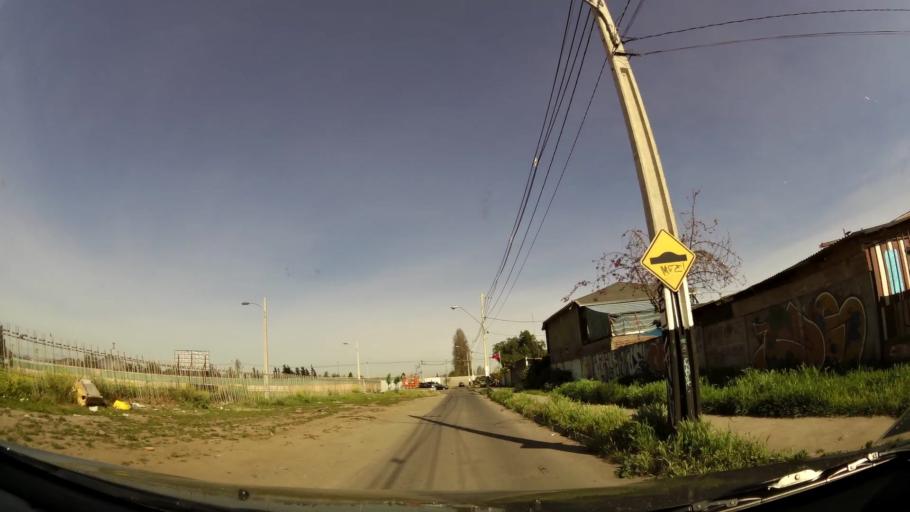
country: CL
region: Santiago Metropolitan
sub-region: Provincia de Cordillera
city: Puente Alto
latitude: -33.6131
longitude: -70.5994
